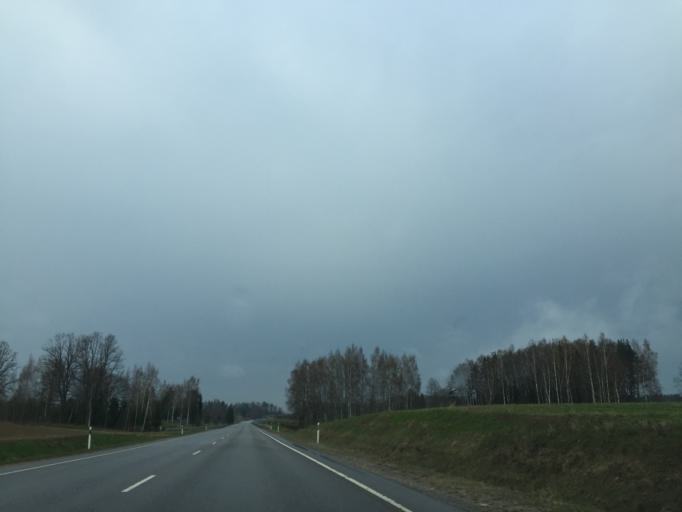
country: EE
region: Tartu
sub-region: UElenurme vald
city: Ulenurme
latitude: 58.1672
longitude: 26.6920
